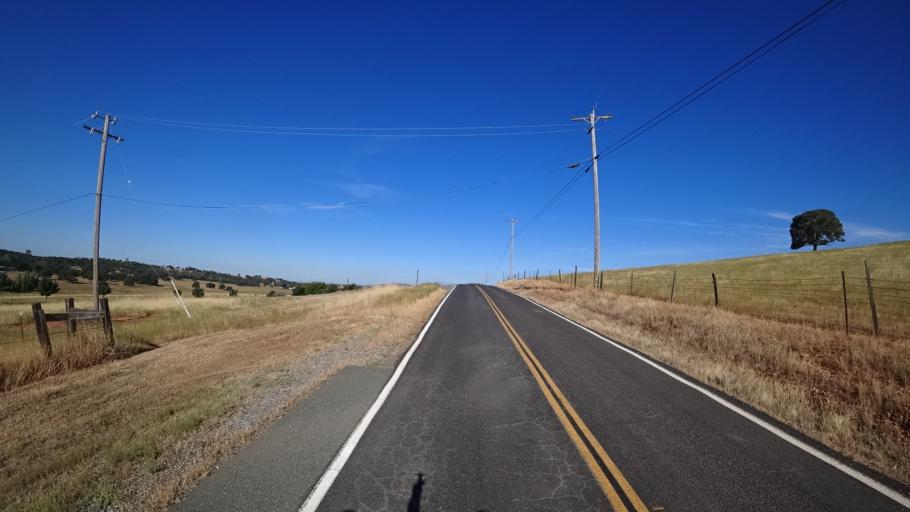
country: US
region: California
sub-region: Calaveras County
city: Valley Springs
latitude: 38.1893
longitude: -120.8017
